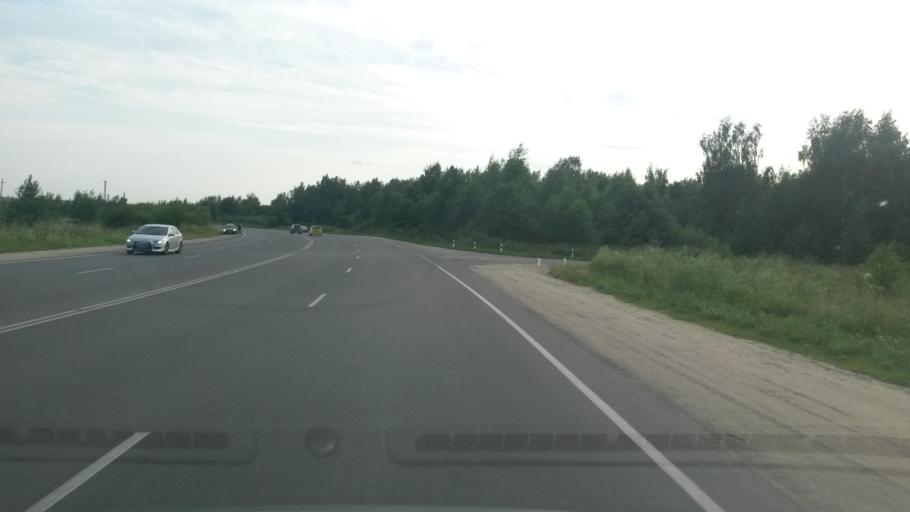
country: RU
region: Ivanovo
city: Novo-Talitsy
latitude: 57.0210
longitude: 40.8917
